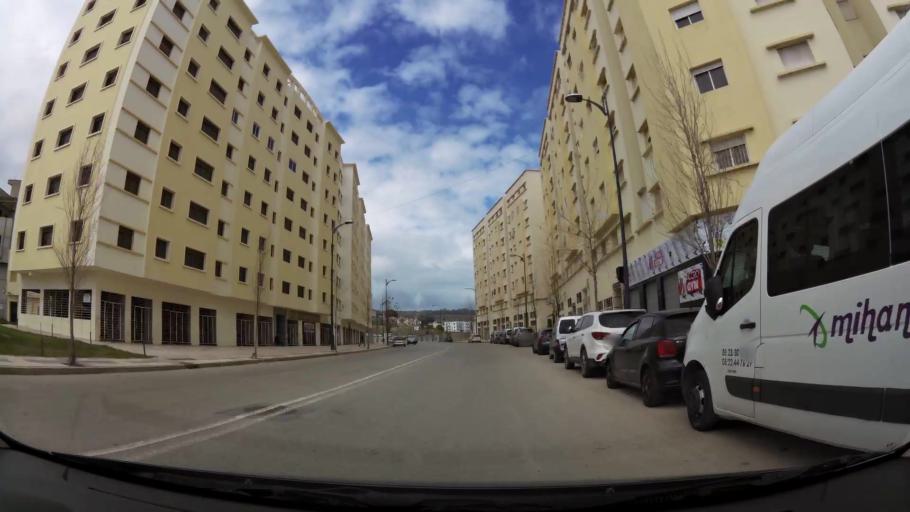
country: MA
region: Tanger-Tetouan
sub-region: Tanger-Assilah
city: Boukhalef
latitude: 35.7658
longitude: -5.8573
